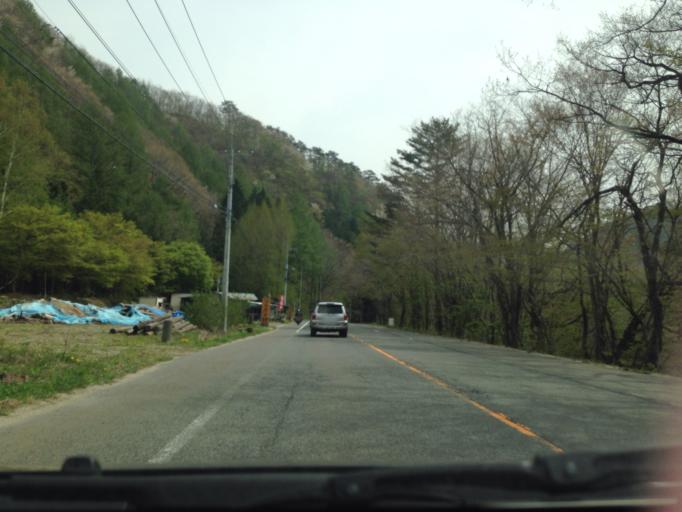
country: JP
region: Tochigi
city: Nikko
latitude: 37.0300
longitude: 139.7278
